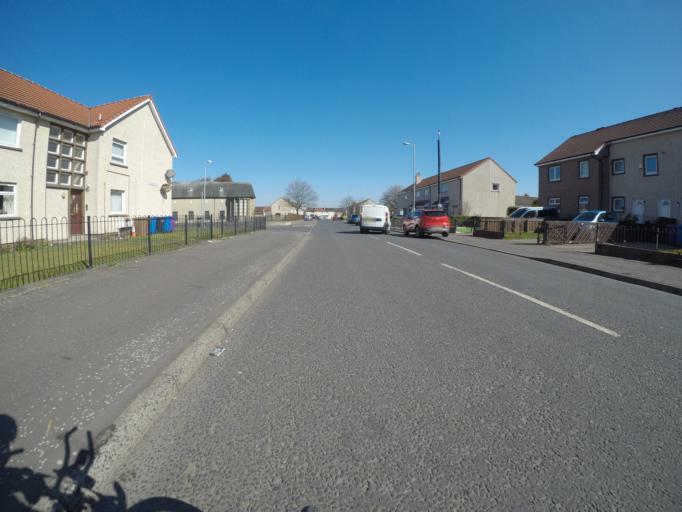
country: GB
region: Scotland
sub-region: North Ayrshire
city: Irvine
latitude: 55.6234
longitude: -4.6608
